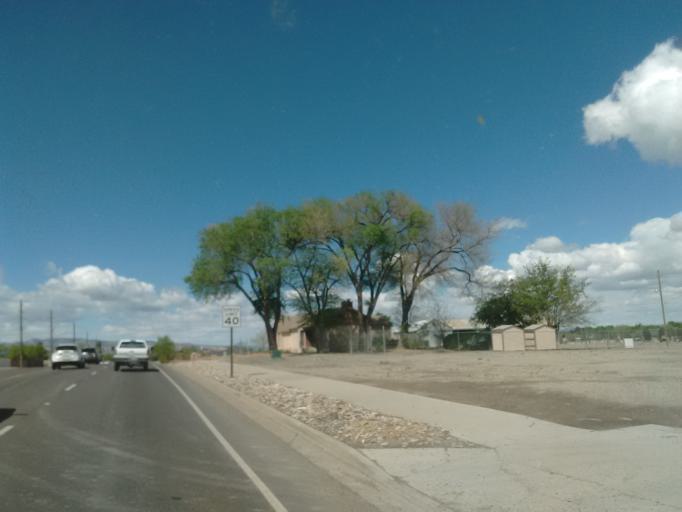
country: US
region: Colorado
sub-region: Mesa County
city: Fruitvale
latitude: 39.0919
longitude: -108.5248
